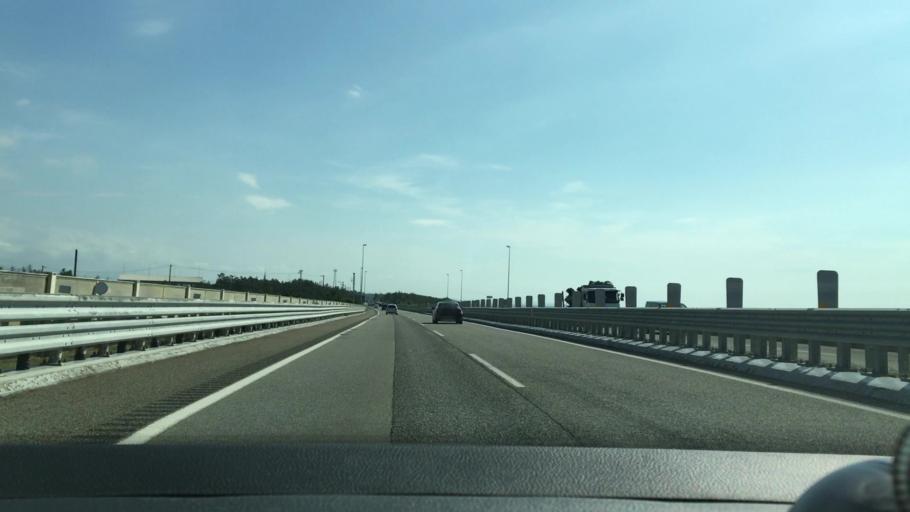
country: JP
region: Ishikawa
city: Komatsu
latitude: 36.4868
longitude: 136.4787
